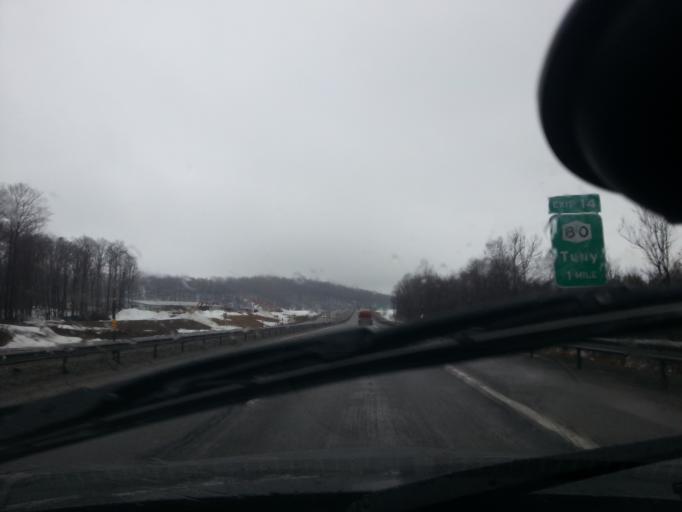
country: US
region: New York
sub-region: Onondaga County
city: Nedrow
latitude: 42.8141
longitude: -76.1244
